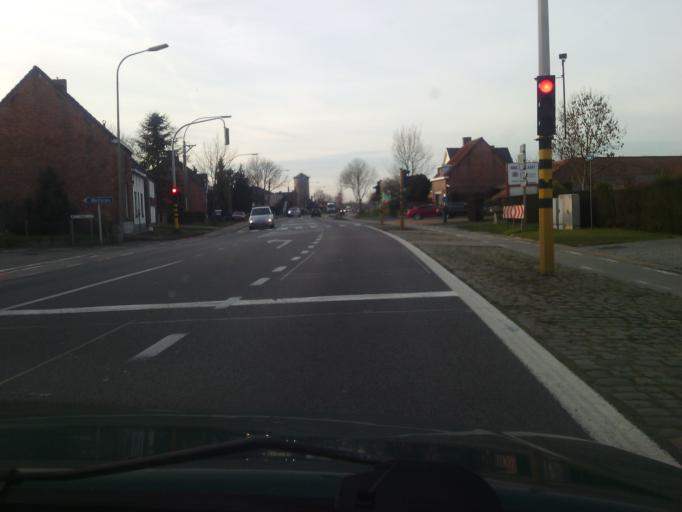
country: BE
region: Flanders
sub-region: Provincie Oost-Vlaanderen
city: Wetteren
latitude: 51.0403
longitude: 3.8927
